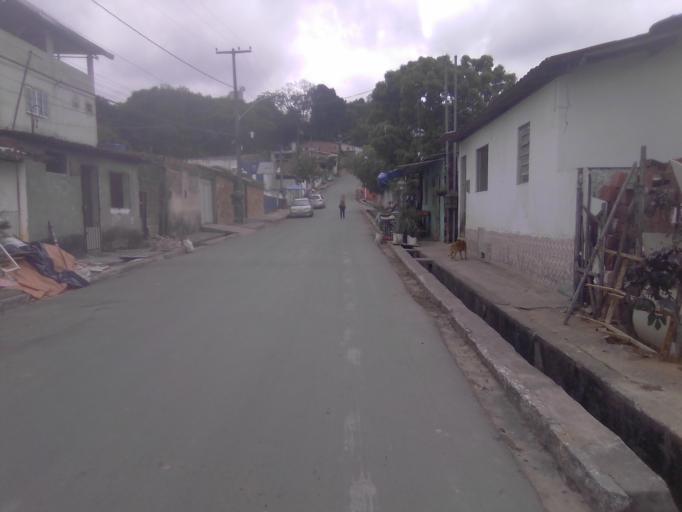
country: BR
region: Pernambuco
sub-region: Jaboatao Dos Guararapes
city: Jaboatao dos Guararapes
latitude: -8.0657
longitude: -35.0010
